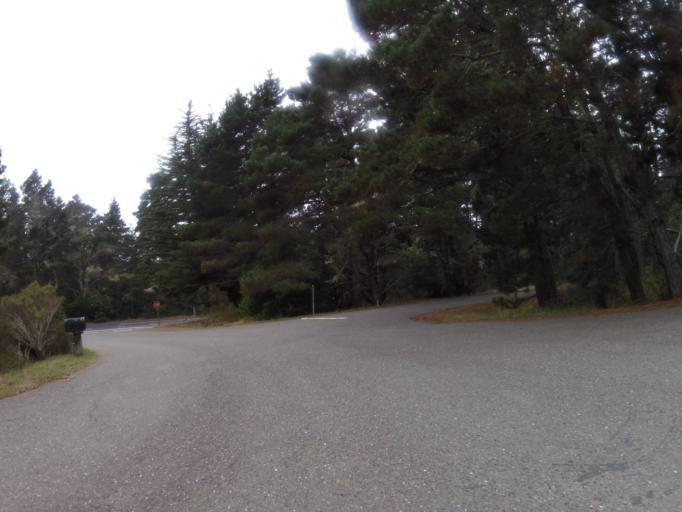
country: US
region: California
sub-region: Sonoma County
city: Sea Ranch
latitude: 38.5696
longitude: -123.3205
